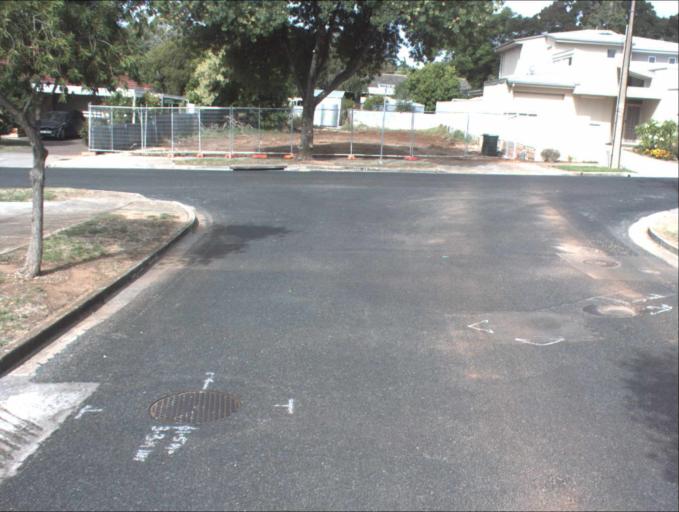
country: AU
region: South Australia
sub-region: Port Adelaide Enfield
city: Blair Athol
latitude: -34.8681
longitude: 138.5974
